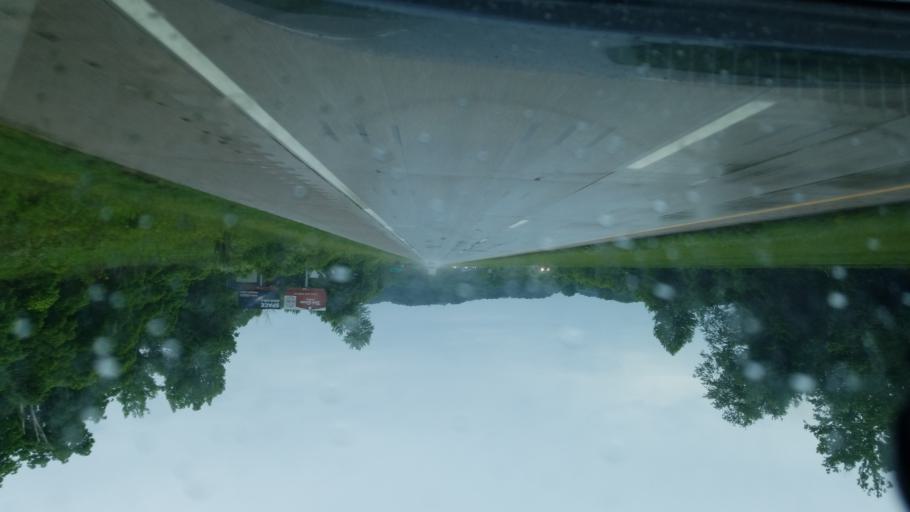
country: US
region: Ohio
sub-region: Athens County
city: Athens
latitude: 39.3260
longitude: -81.9975
